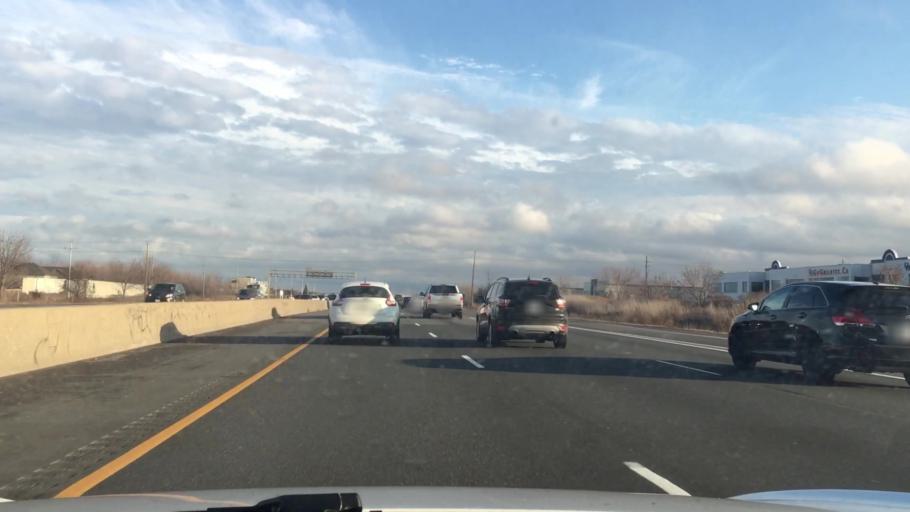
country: CA
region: Ontario
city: Hamilton
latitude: 43.2297
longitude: -79.6886
